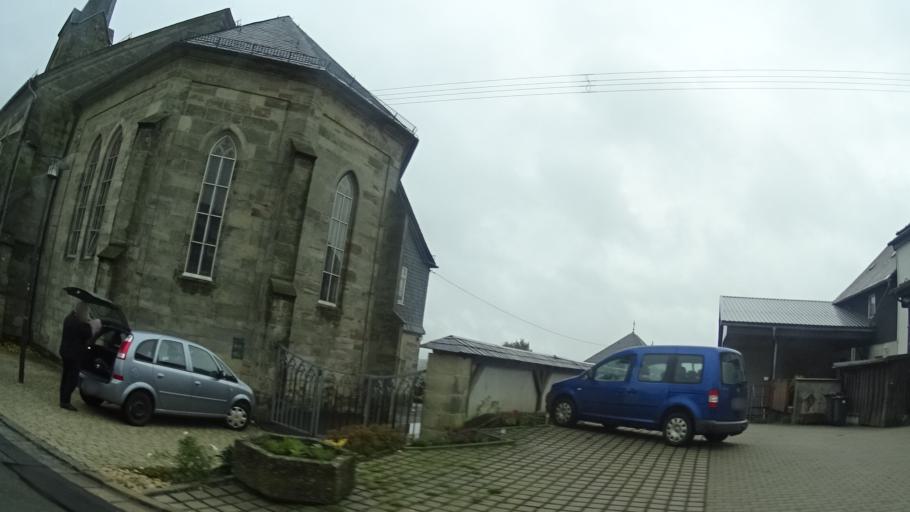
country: DE
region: Bavaria
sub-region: Upper Franconia
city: Tschirn
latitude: 50.3999
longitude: 11.4471
